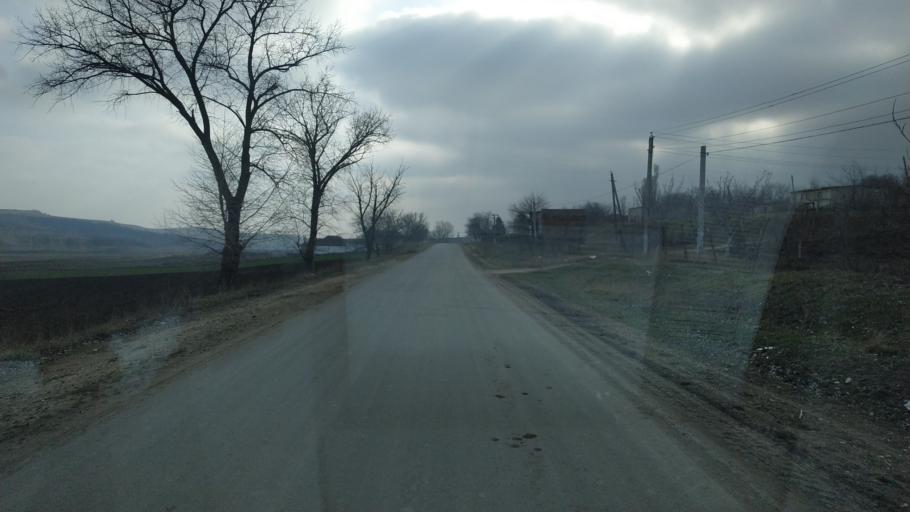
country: MD
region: Nisporeni
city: Nisporeni
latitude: 46.9327
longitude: 28.3282
